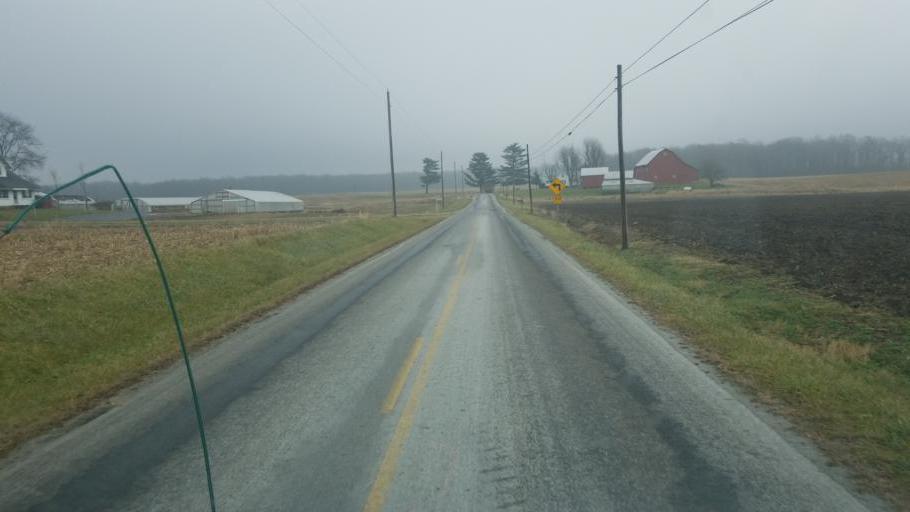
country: US
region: Ohio
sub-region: Hardin County
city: Kenton
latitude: 40.5646
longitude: -83.4800
